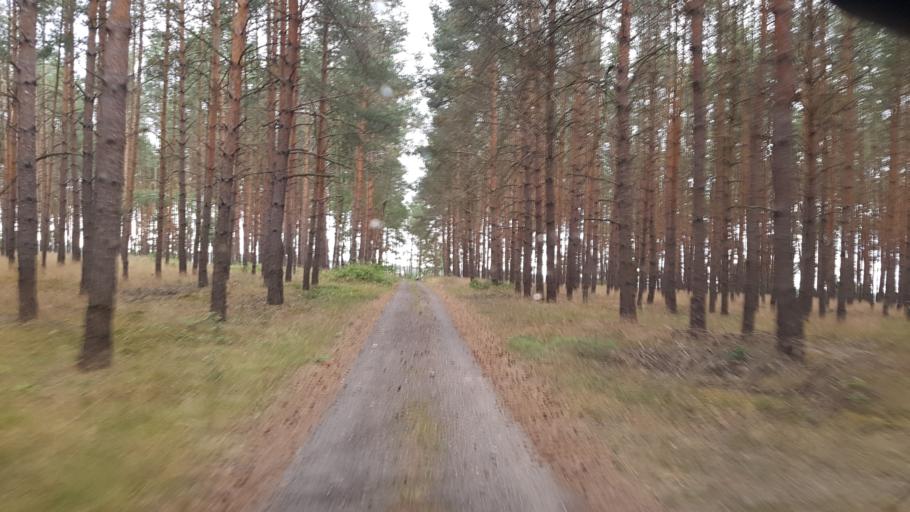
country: DE
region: Brandenburg
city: Sonnewalde
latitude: 51.7143
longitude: 13.7044
